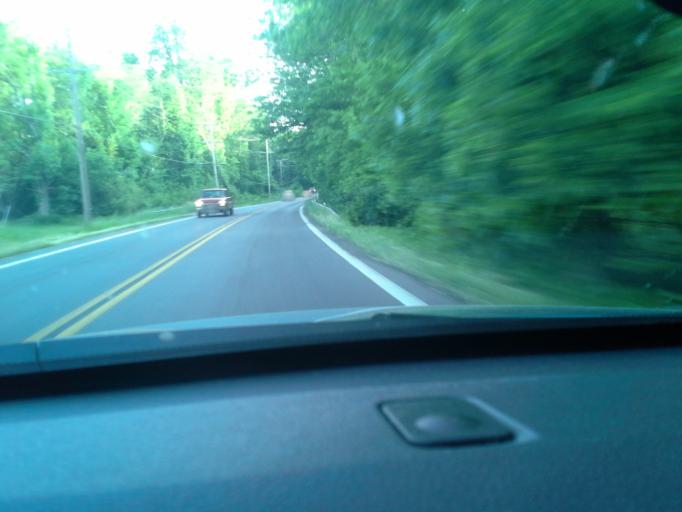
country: US
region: Maryland
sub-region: Anne Arundel County
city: Shady Side
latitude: 38.8476
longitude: -76.5582
